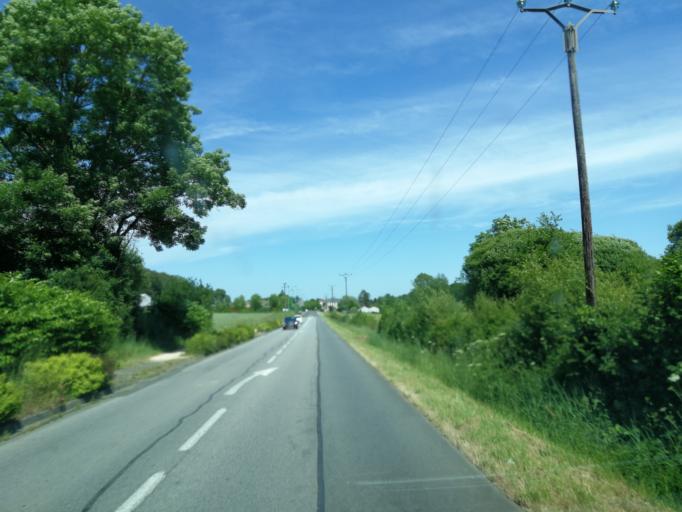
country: FR
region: Poitou-Charentes
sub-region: Departement des Deux-Sevres
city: Courlay
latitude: 46.8077
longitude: -0.5662
